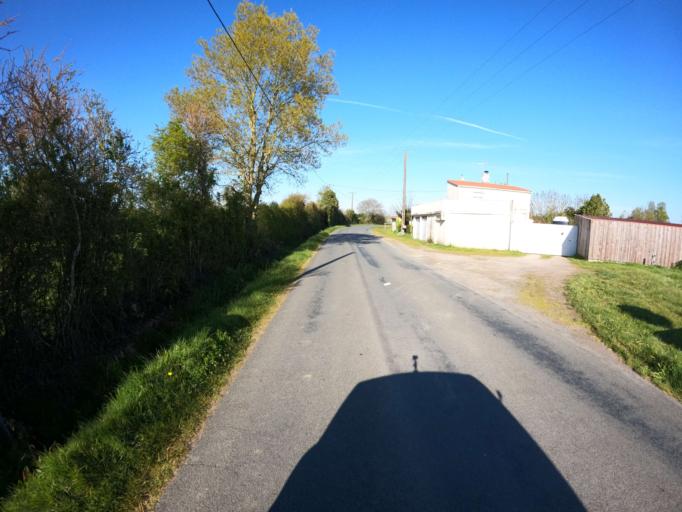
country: FR
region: Pays de la Loire
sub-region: Departement de la Vendee
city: Les Brouzils
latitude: 46.8908
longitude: -1.3079
